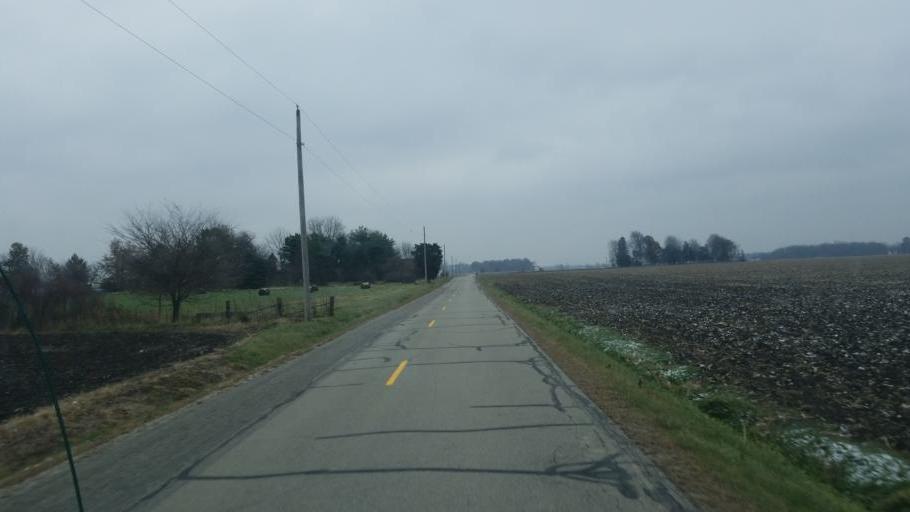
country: US
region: Ohio
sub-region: Crawford County
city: Crestline
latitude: 40.8286
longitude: -82.7597
